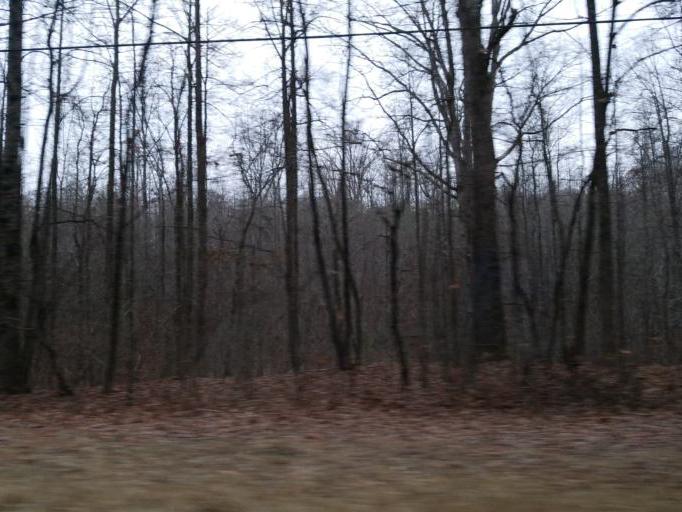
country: US
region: Georgia
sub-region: Dawson County
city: Dawsonville
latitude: 34.4647
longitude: -84.1472
